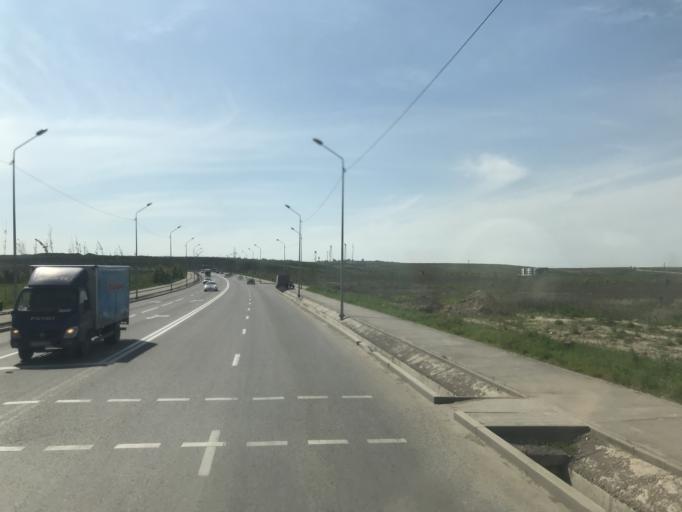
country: KZ
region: Almaty Oblysy
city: Burunday
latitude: 43.3137
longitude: 76.8422
